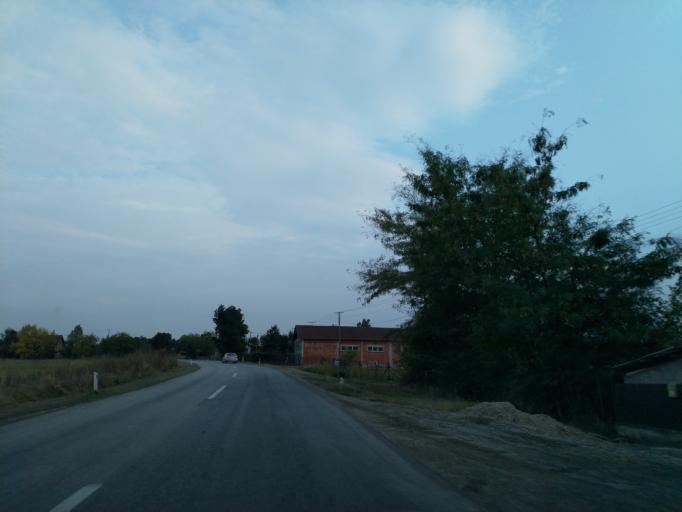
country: RS
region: Central Serbia
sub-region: Sumadijski Okrug
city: Kragujevac
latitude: 44.1081
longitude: 20.8416
